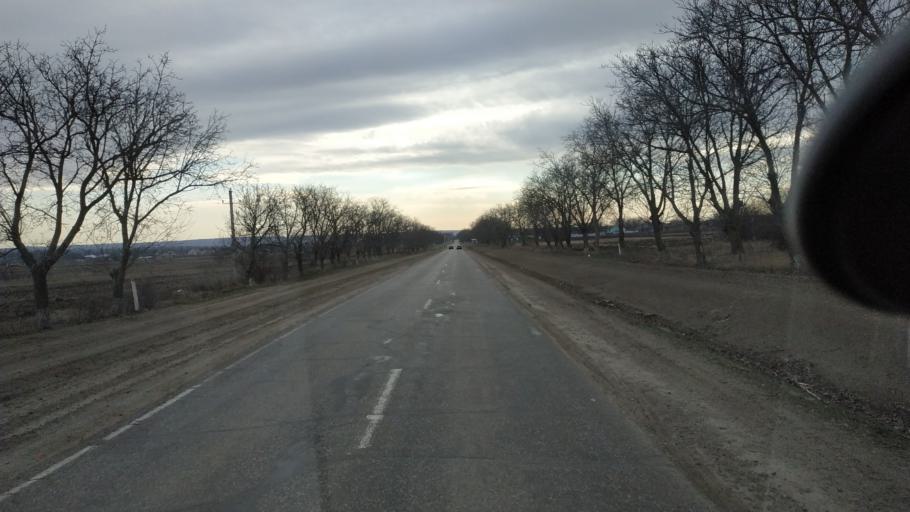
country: MD
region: Criuleni
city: Criuleni
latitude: 47.1742
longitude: 29.1307
